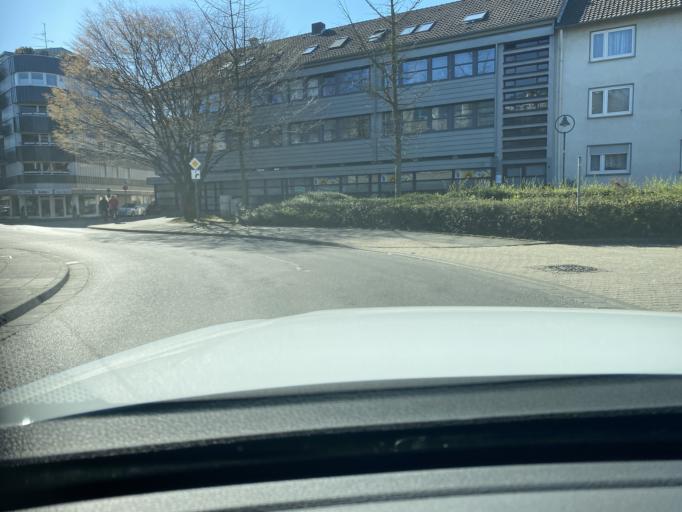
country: DE
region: North Rhine-Westphalia
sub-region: Regierungsbezirk Dusseldorf
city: Grevenbroich
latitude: 51.0928
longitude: 6.5810
